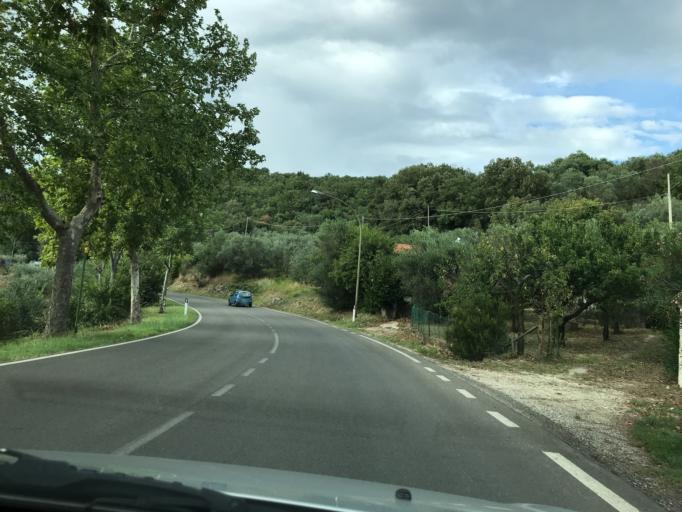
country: IT
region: Umbria
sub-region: Provincia di Terni
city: Guardea
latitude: 42.6297
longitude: 12.2965
